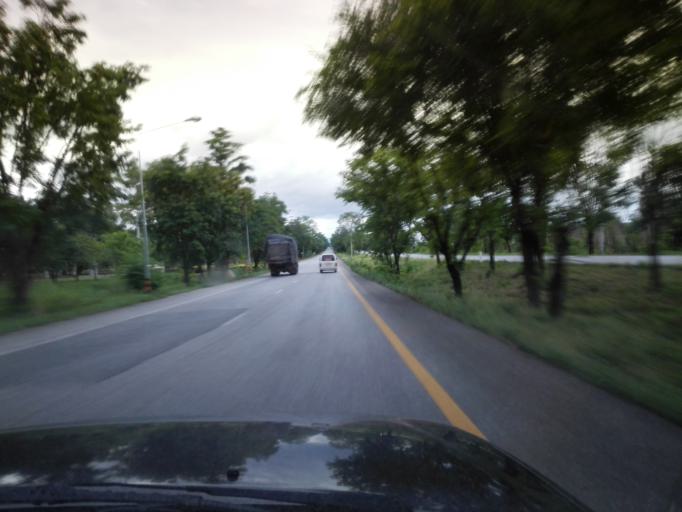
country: TH
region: Tak
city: Tak
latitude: 16.8103
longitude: 99.1401
